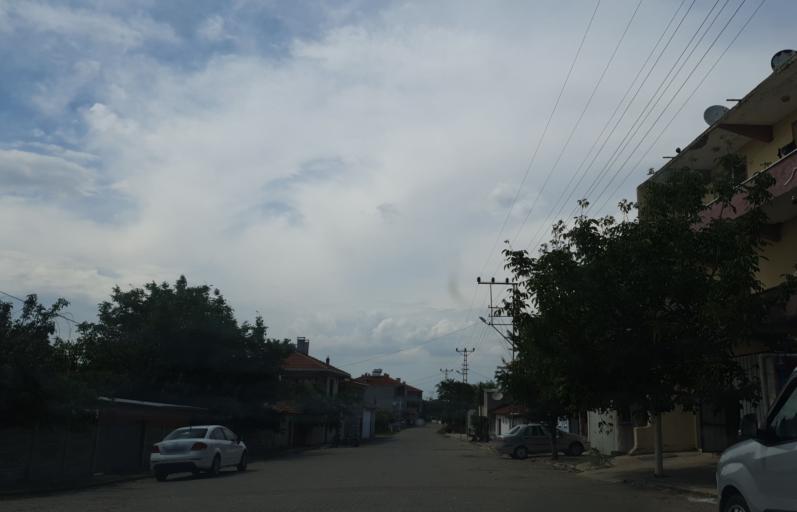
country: TR
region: Tekirdag
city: Muratli
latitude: 41.2181
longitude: 27.5480
